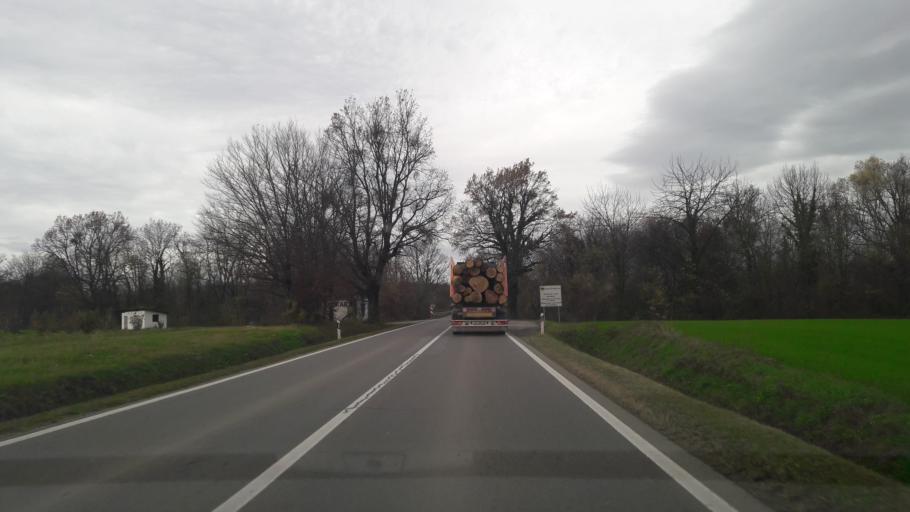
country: HR
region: Virovitick-Podravska
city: Orahovica
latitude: 45.5416
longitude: 17.9207
